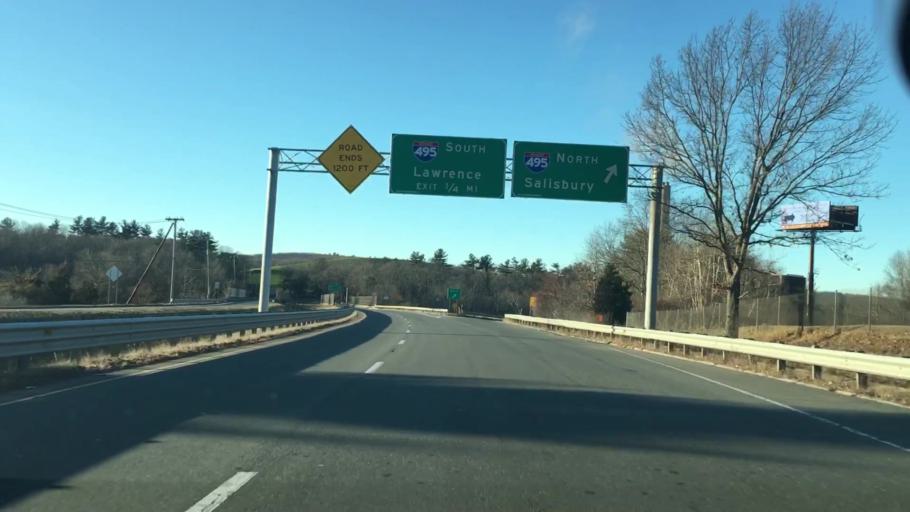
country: US
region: Massachusetts
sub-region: Essex County
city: Haverhill
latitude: 42.7608
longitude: -71.1194
